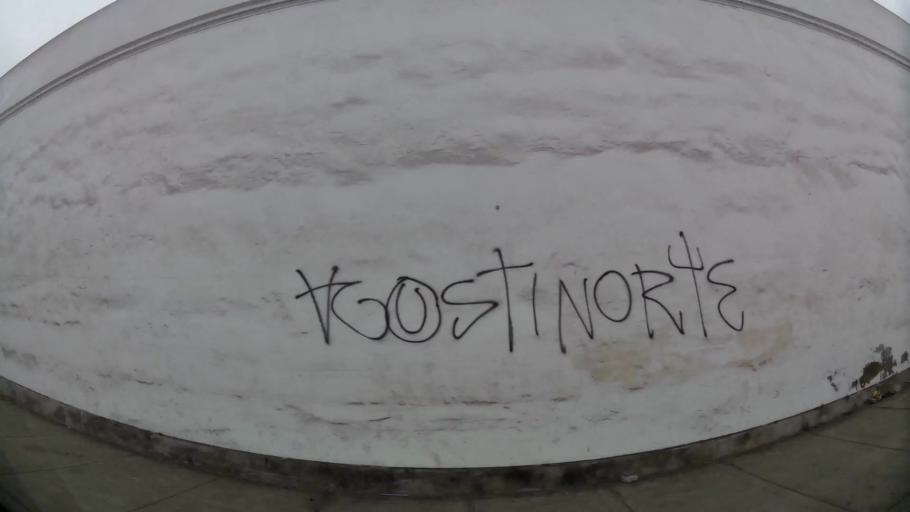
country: PE
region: Lima
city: Lima
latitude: -12.0410
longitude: -77.0050
